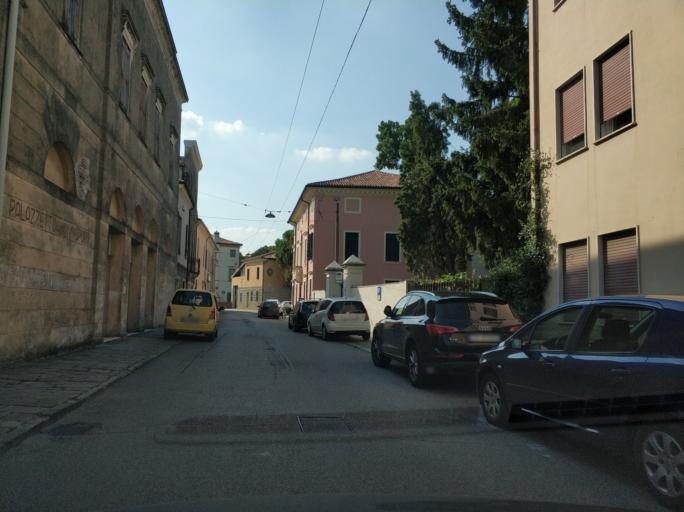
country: IT
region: Veneto
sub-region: Provincia di Padova
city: Este
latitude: 45.2304
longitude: 11.6524
